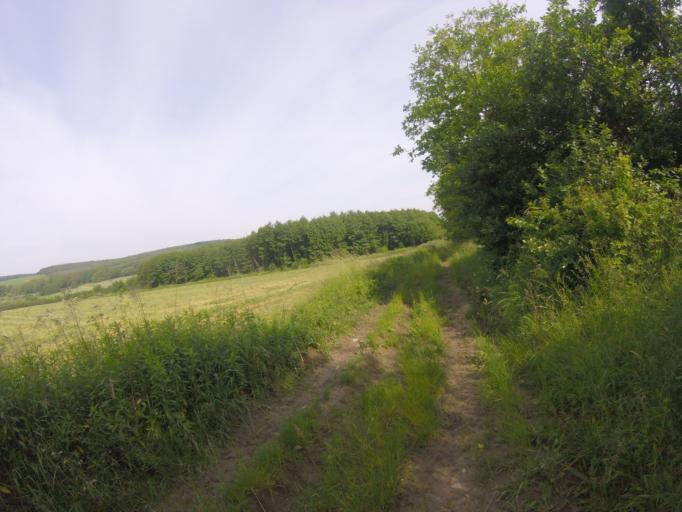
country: HU
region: Zala
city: Zalaszentgrot
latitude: 46.9065
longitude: 17.1573
